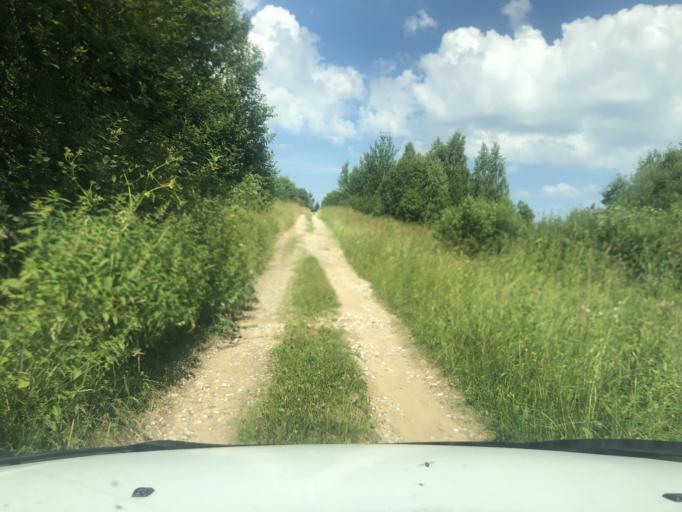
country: RU
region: Jaroslavl
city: Pereslavl'-Zalesskiy
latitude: 57.0436
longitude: 38.8732
